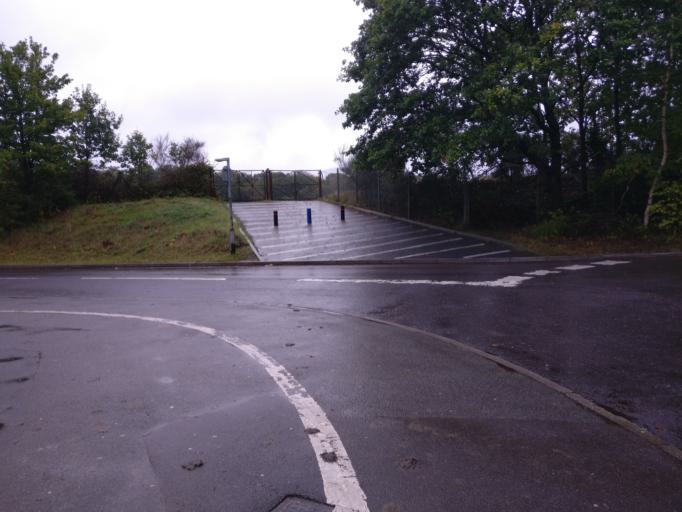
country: GB
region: England
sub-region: Surrey
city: Frimley
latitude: 51.3205
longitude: -0.7229
